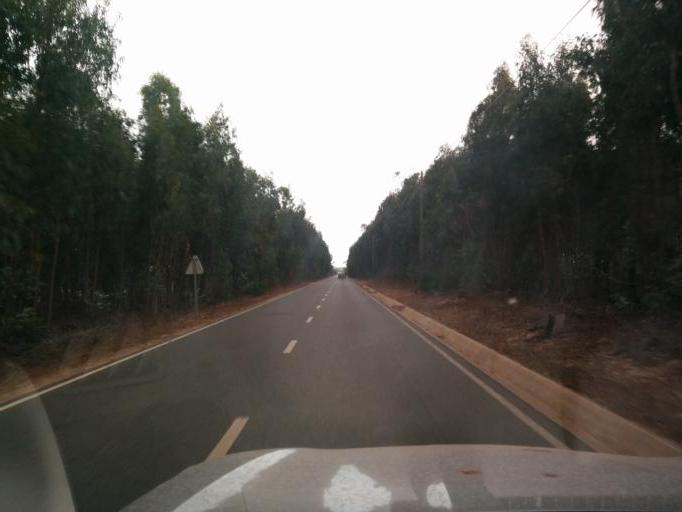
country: PT
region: Beja
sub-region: Odemira
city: Sao Teotonio
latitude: 37.5637
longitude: -8.7361
